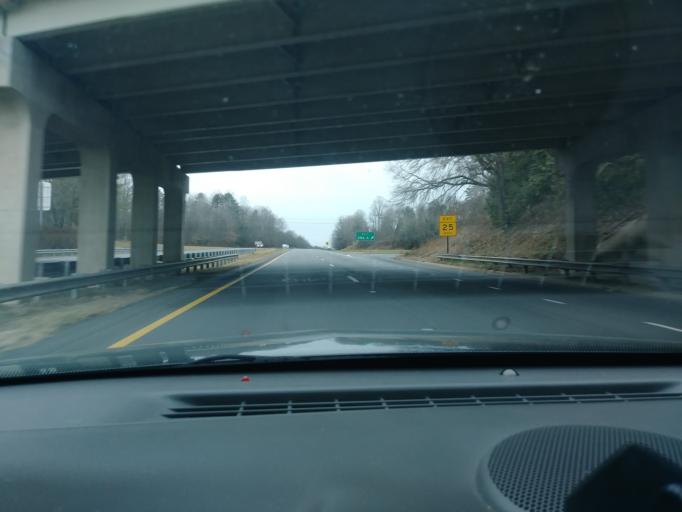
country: US
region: North Carolina
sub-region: Wilkes County
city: Wilkesboro
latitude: 36.1368
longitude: -81.1610
